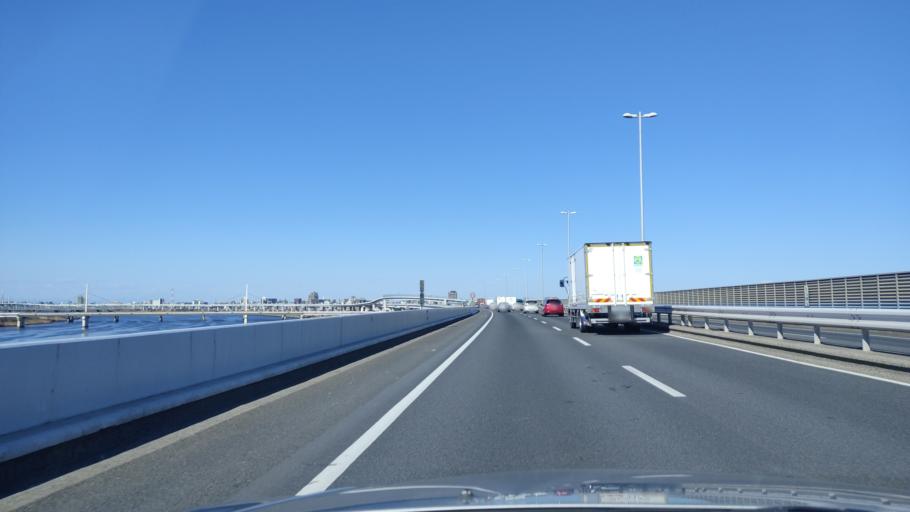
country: JP
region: Tokyo
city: Urayasu
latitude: 35.6918
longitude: 139.8625
